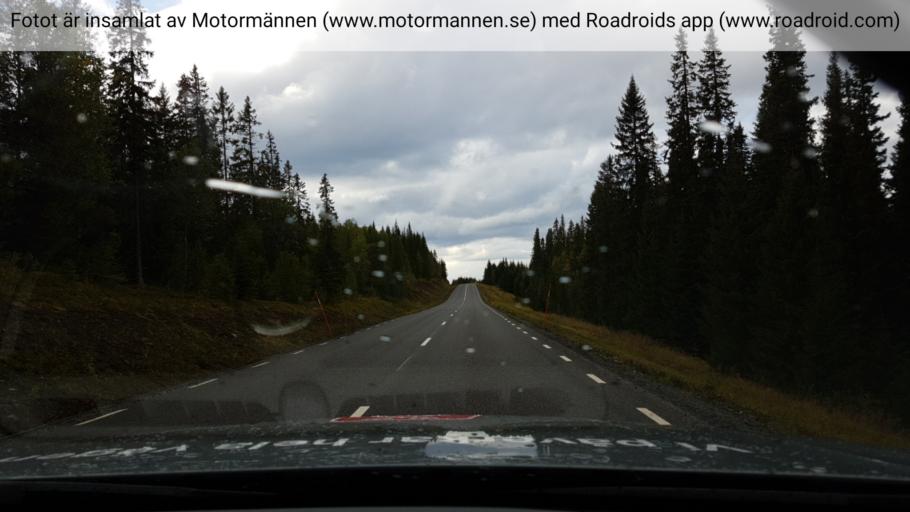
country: SE
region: Jaemtland
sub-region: Are Kommun
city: Are
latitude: 63.6045
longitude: 13.1508
